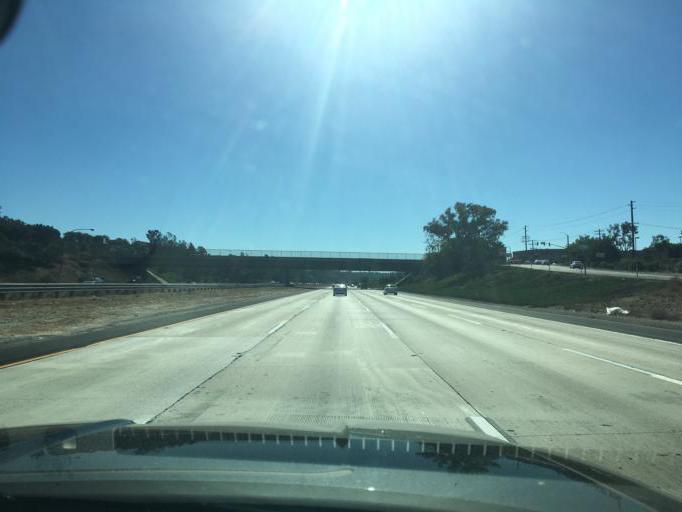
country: US
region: California
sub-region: San Diego County
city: La Mesa
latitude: 32.8123
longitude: -117.1145
